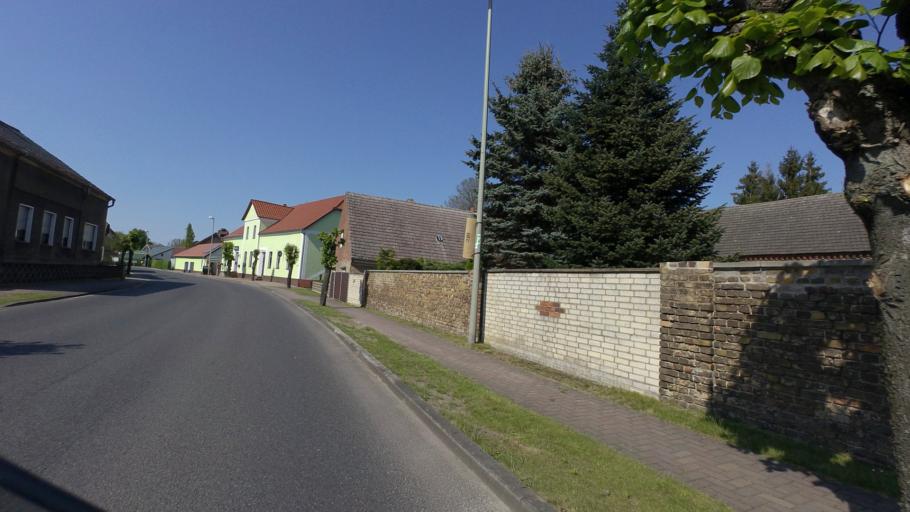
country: DE
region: Brandenburg
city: Schlepzig
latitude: 52.0802
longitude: 13.8779
